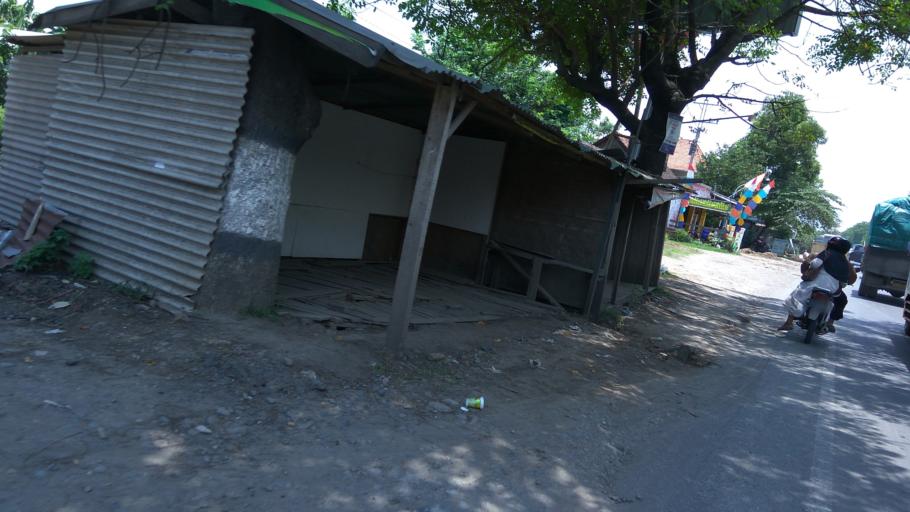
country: ID
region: Central Java
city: Mranggen
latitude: -7.0295
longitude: 110.5328
